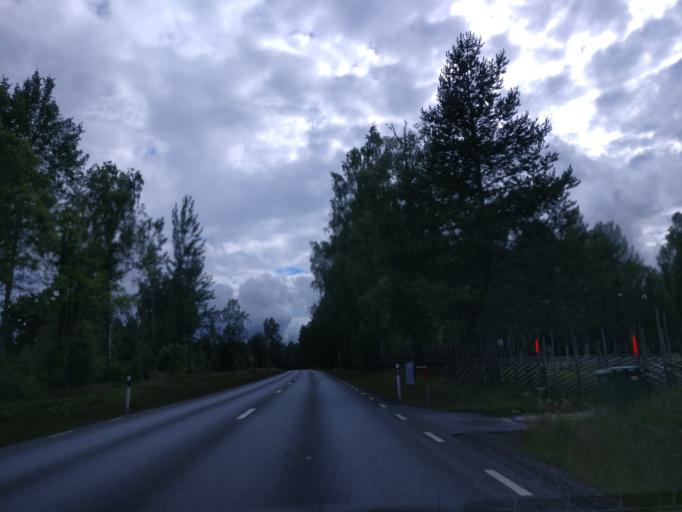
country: SE
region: Vaermland
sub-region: Hagfors Kommun
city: Hagfors
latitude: 59.9796
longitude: 13.5705
